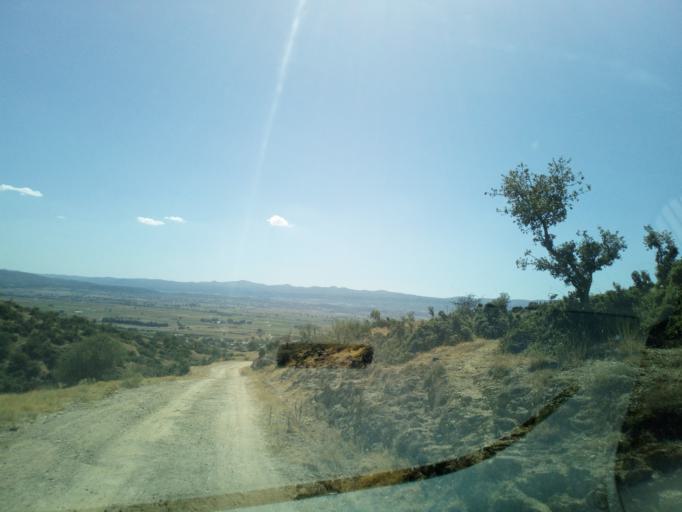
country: GR
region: Central Macedonia
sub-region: Nomos Thessalonikis
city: Gerakarou
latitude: 40.7050
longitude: 23.2175
